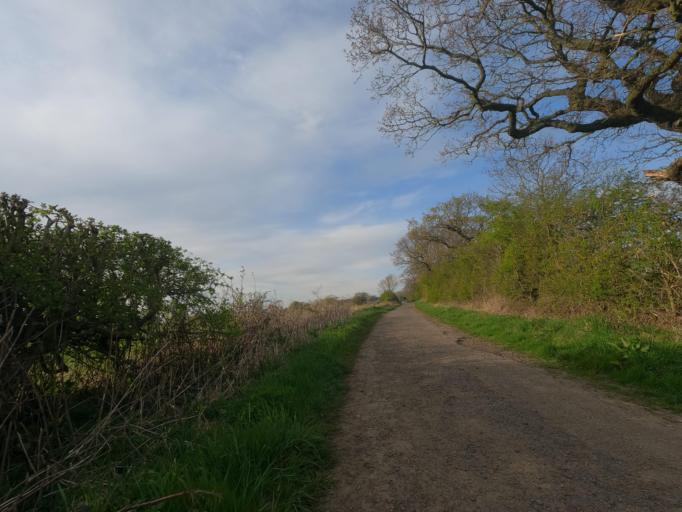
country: GB
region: England
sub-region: Northumberland
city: Cramlington
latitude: 55.0812
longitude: -1.6091
